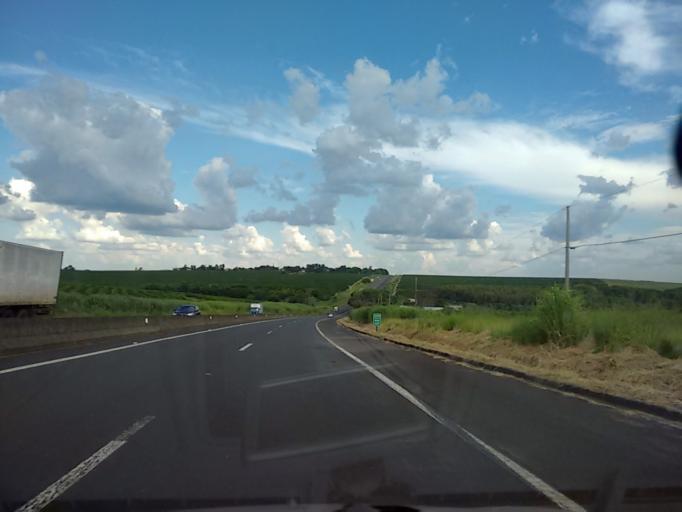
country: BR
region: Sao Paulo
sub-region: Marilia
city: Marilia
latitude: -22.2163
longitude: -49.8403
